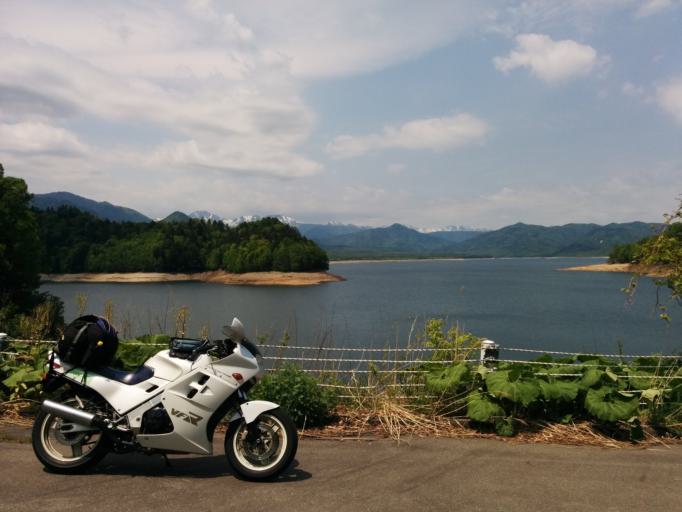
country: JP
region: Hokkaido
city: Otofuke
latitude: 43.3731
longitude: 143.2188
